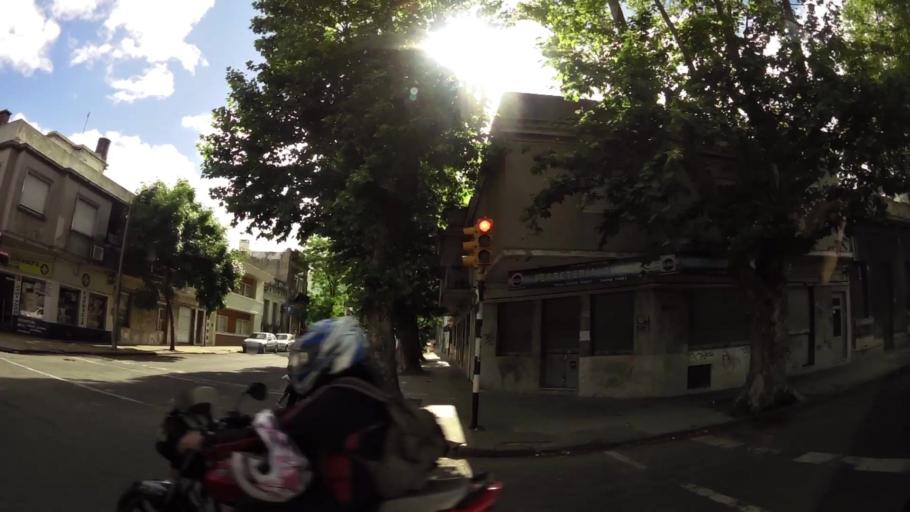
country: UY
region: Montevideo
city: Montevideo
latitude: -34.8928
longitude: -56.1787
